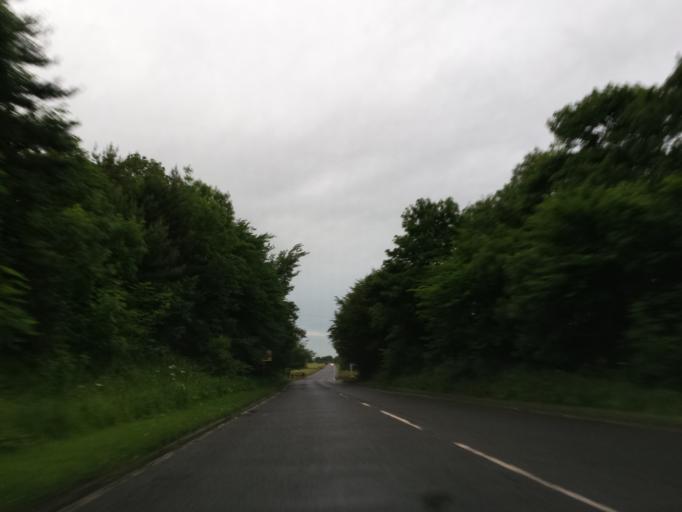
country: GB
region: Scotland
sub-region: East Lothian
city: Dunbar
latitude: 55.9908
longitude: -2.5732
